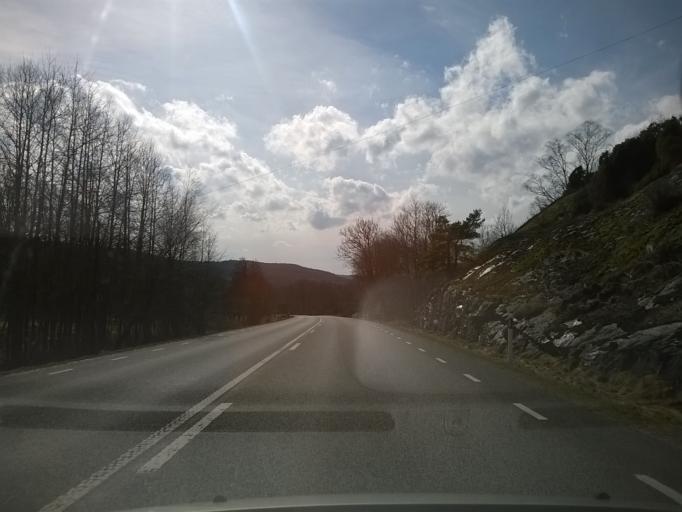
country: SE
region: Vaestra Goetaland
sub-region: Orust
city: Henan
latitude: 58.2819
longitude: 11.6957
